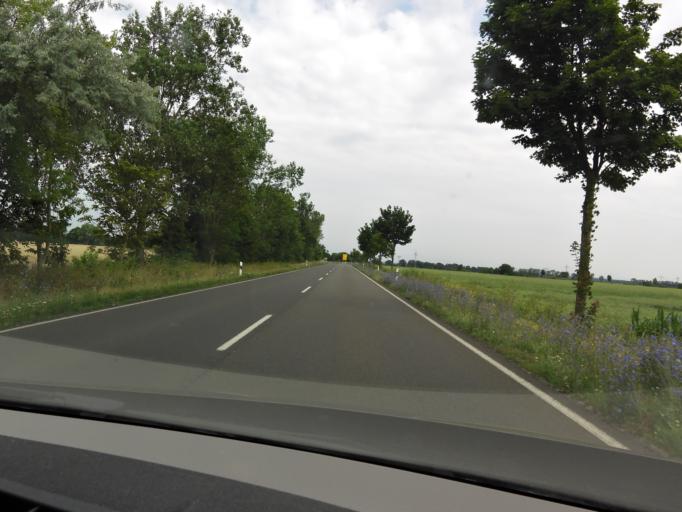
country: DE
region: Saxony-Anhalt
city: Kemberg
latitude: 51.8023
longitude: 12.6519
